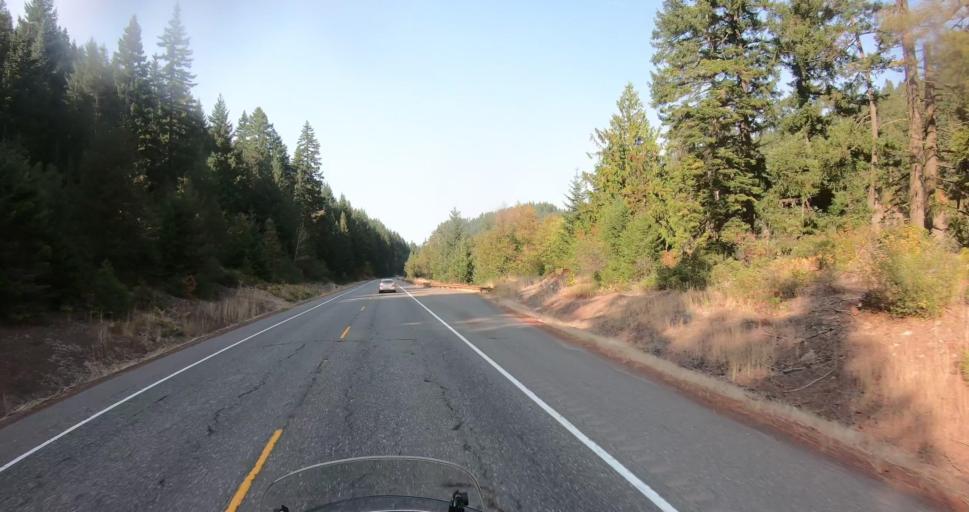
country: US
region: Oregon
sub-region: Hood River County
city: Odell
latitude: 45.4338
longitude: -121.5753
